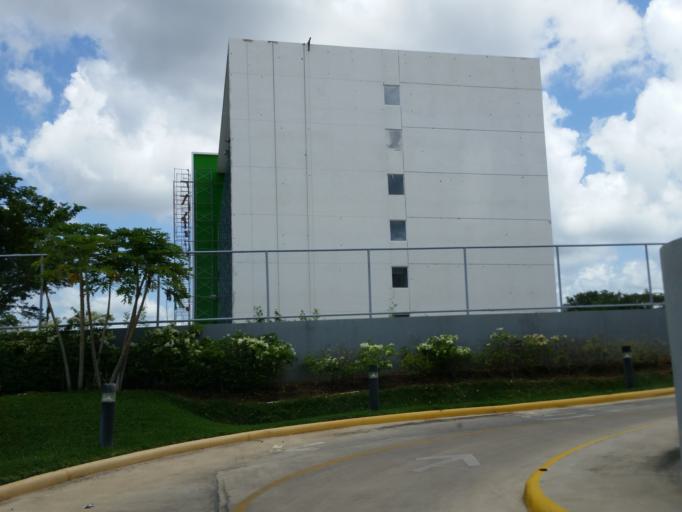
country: NI
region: Managua
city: Managua
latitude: 12.1036
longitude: -86.2566
